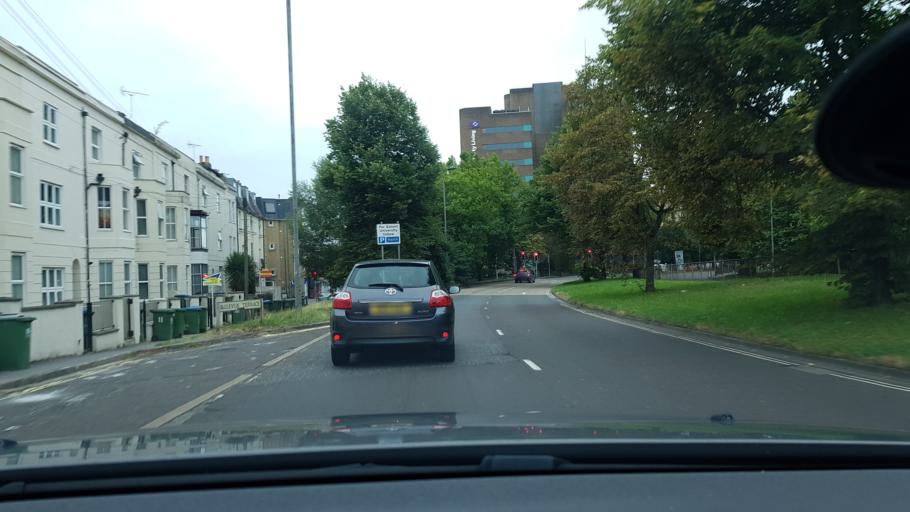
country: GB
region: England
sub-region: Southampton
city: Southampton
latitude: 50.9135
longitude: -1.4006
